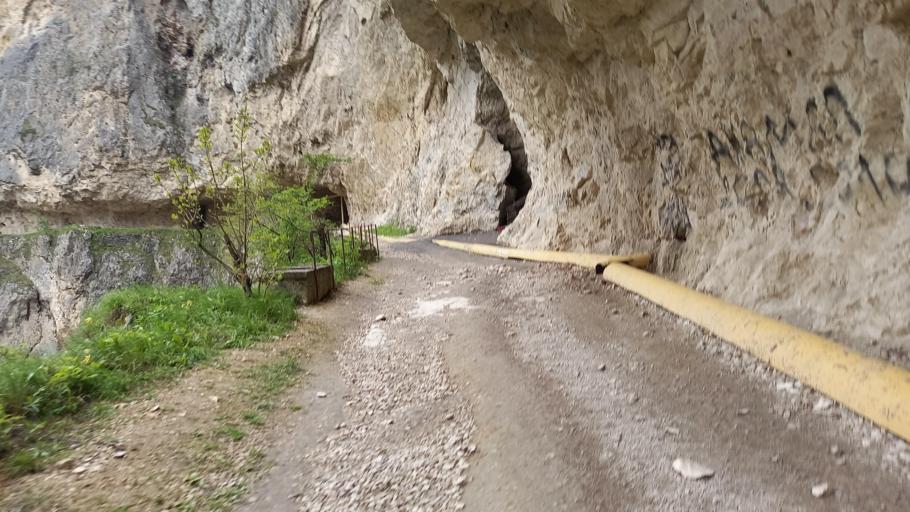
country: RU
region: Kabardino-Balkariya
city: Verkhnyaya Balkariya
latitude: 43.1899
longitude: 43.5174
